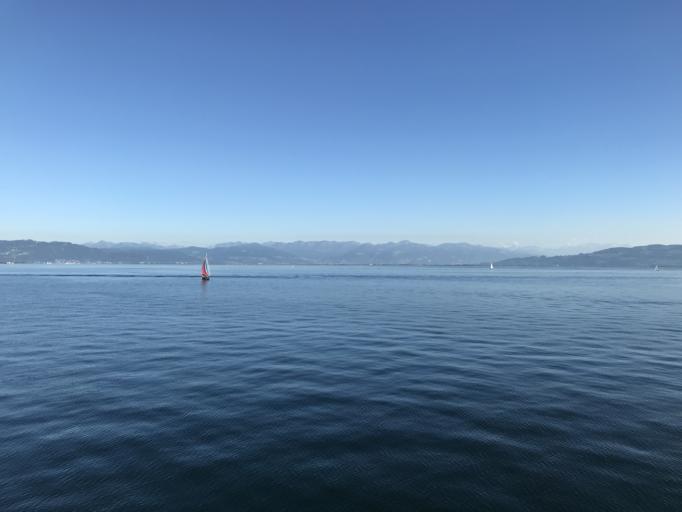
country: DE
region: Baden-Wuerttemberg
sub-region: Tuebingen Region
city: Kressbronn am Bodensee
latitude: 47.5802
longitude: 9.5709
